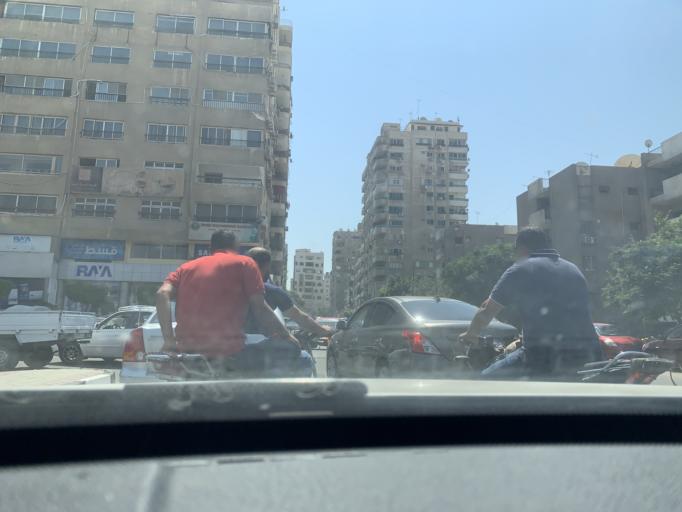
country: EG
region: Muhafazat al Qahirah
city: Cairo
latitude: 30.0491
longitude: 31.3470
